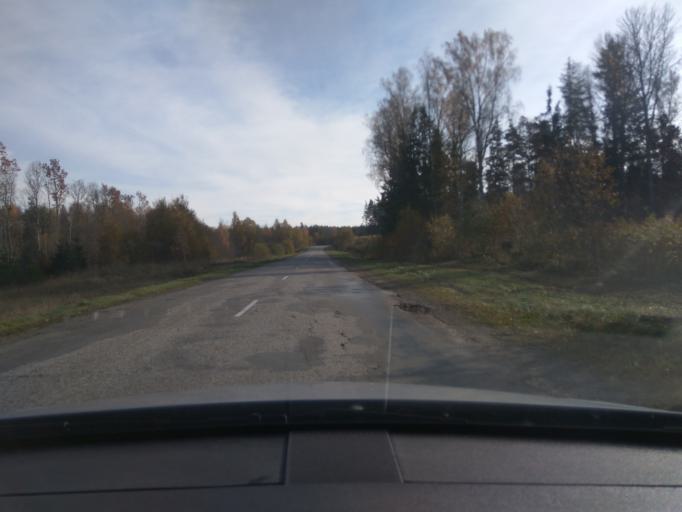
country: LV
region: Alsunga
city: Alsunga
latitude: 57.0108
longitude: 21.7136
